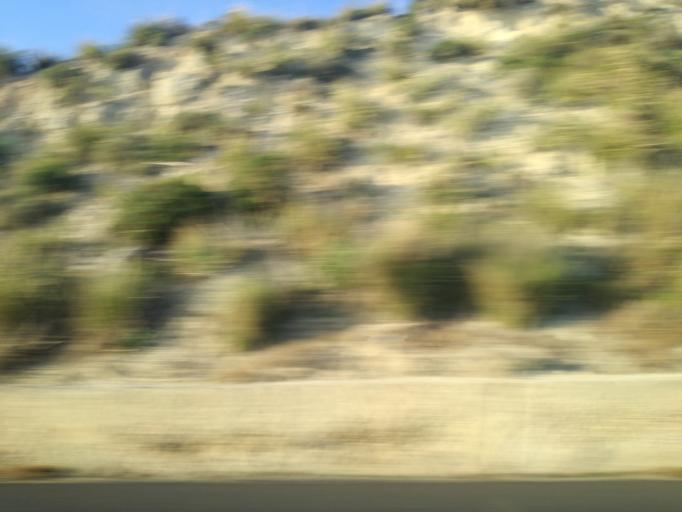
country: IT
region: Sicily
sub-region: Catania
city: San Michele di Ganzaria
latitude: 37.2155
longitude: 14.4209
